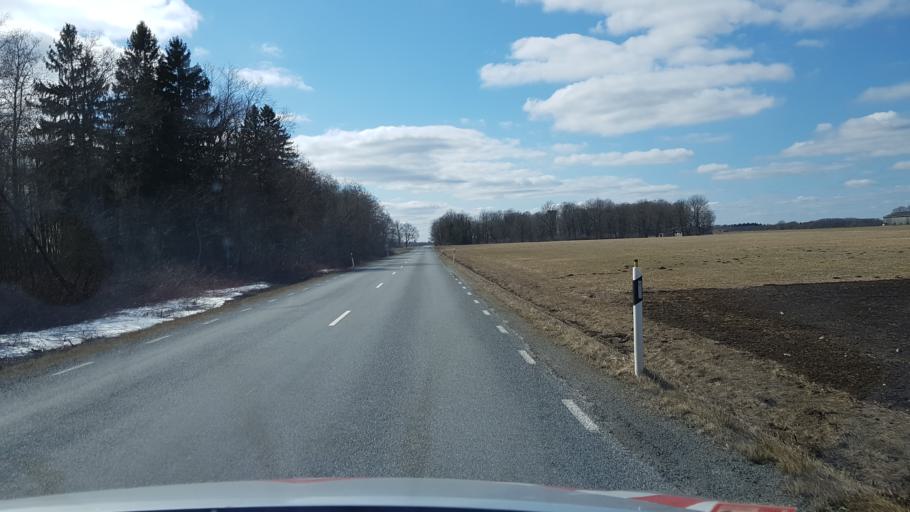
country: EE
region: Laeaene-Virumaa
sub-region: Tapa vald
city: Tapa
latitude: 59.2747
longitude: 25.8703
